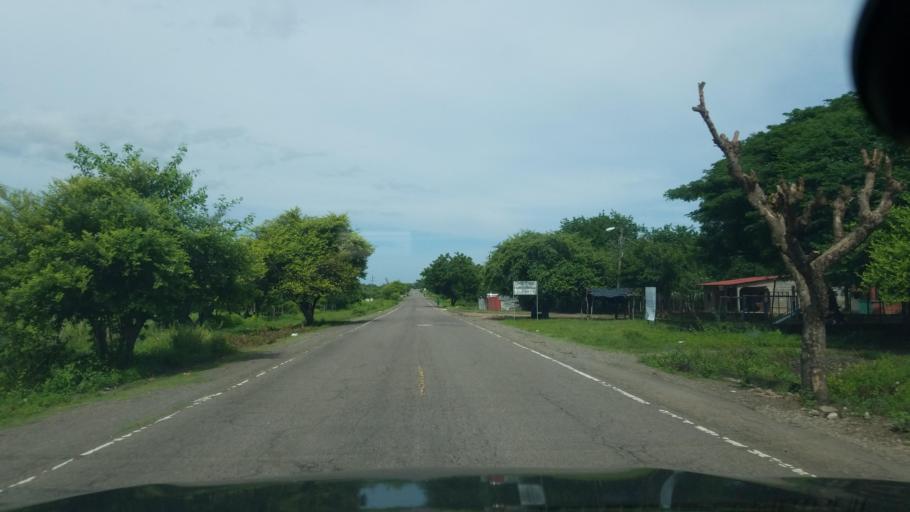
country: HN
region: Choluteca
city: Santa Ana de Yusguare
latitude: 13.3630
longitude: -87.0869
